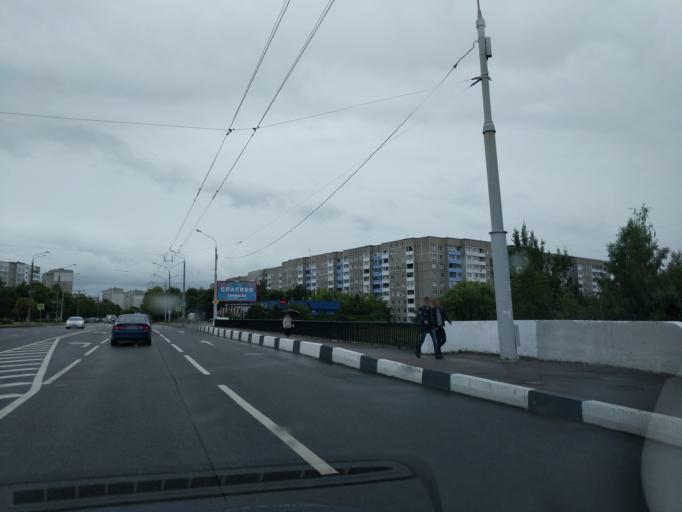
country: BY
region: Minsk
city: Novoye Medvezhino
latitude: 53.8586
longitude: 27.4716
